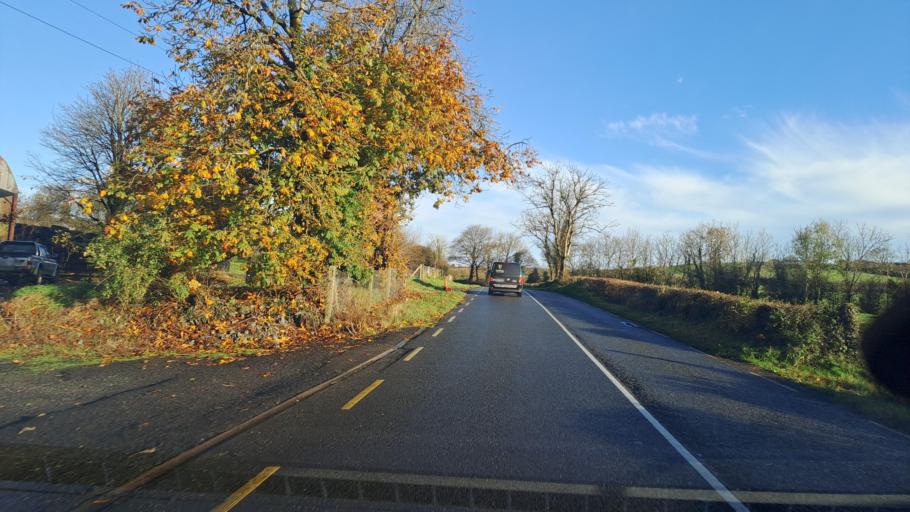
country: IE
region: Ulster
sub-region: County Monaghan
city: Monaghan
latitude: 54.1778
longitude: -6.9959
